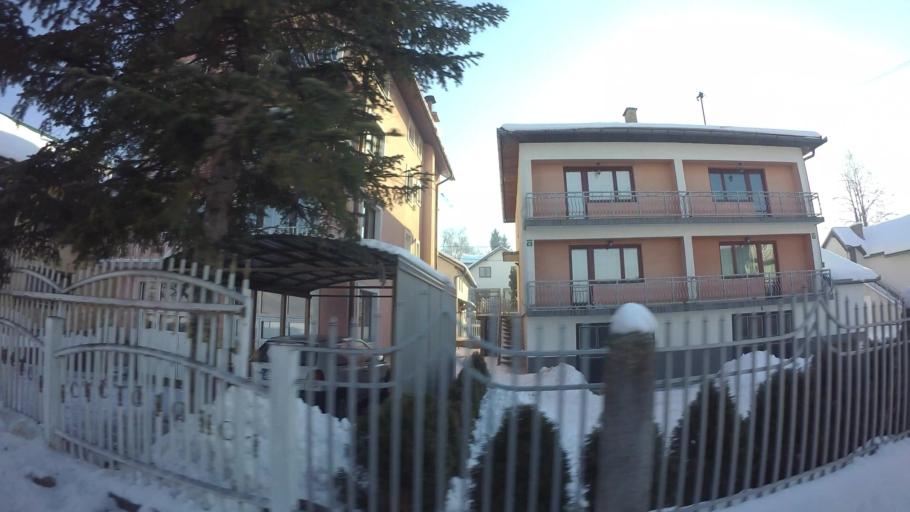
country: BA
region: Federation of Bosnia and Herzegovina
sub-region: Kanton Sarajevo
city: Sarajevo
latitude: 43.8219
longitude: 18.3281
